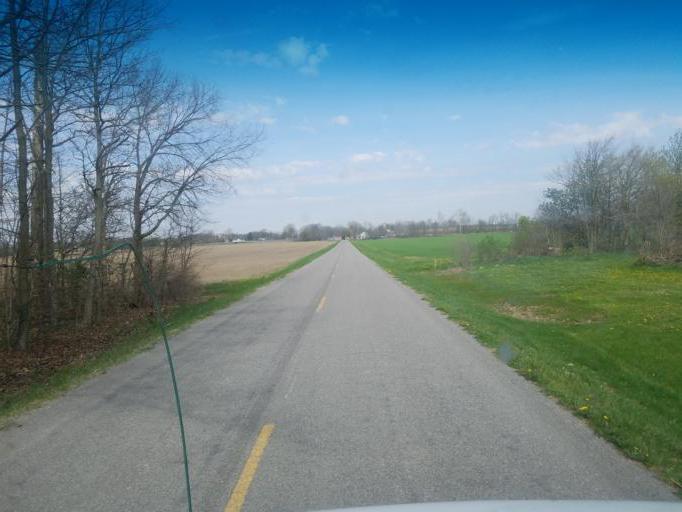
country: US
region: Ohio
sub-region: Logan County
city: Northwood
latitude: 40.4940
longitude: -83.6253
